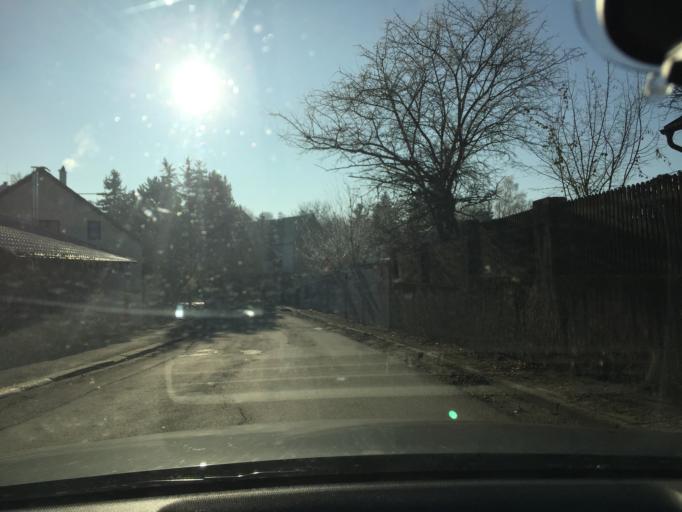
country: CZ
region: Central Bohemia
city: Trebotov
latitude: 49.9966
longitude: 14.2634
